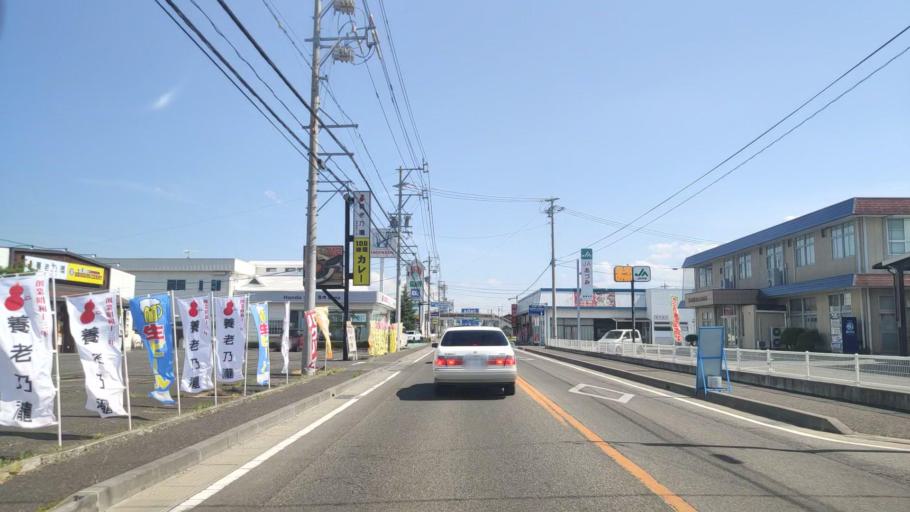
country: JP
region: Nagano
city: Hotaka
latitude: 36.3351
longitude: 137.8900
